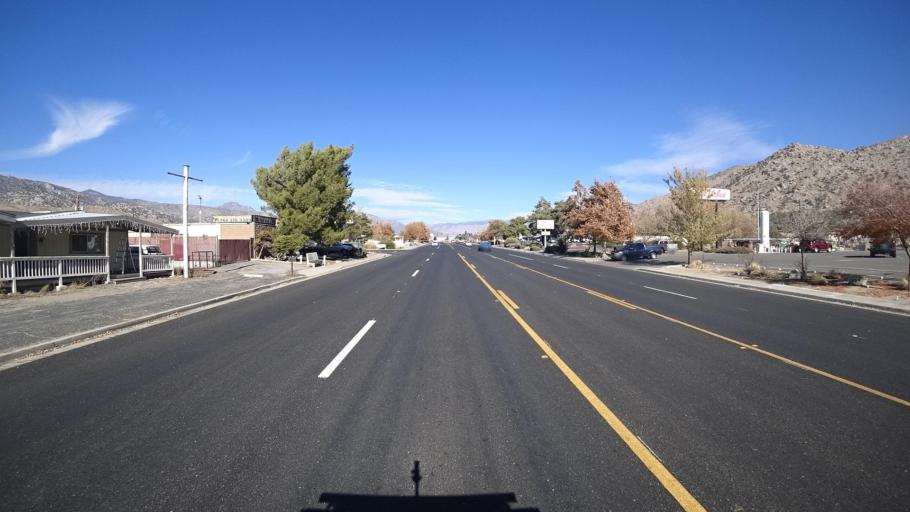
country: US
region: California
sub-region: Kern County
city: Lake Isabella
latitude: 35.6244
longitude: -118.4727
